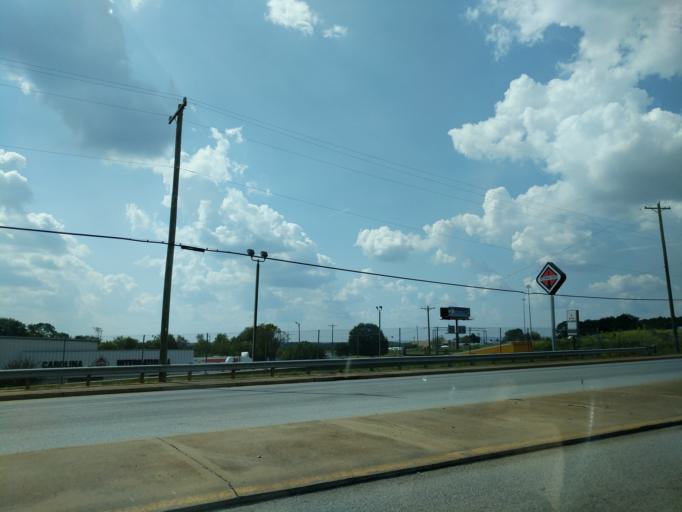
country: US
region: South Carolina
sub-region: Greenville County
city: Five Forks
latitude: 34.8703
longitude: -82.2233
